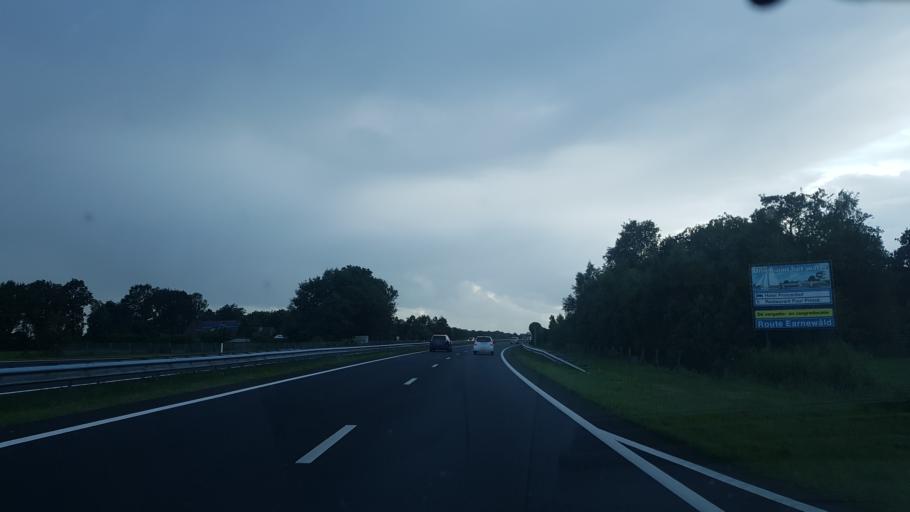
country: NL
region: Friesland
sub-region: Gemeente Smallingerland
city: Oudega
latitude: 53.1453
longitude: 5.9950
